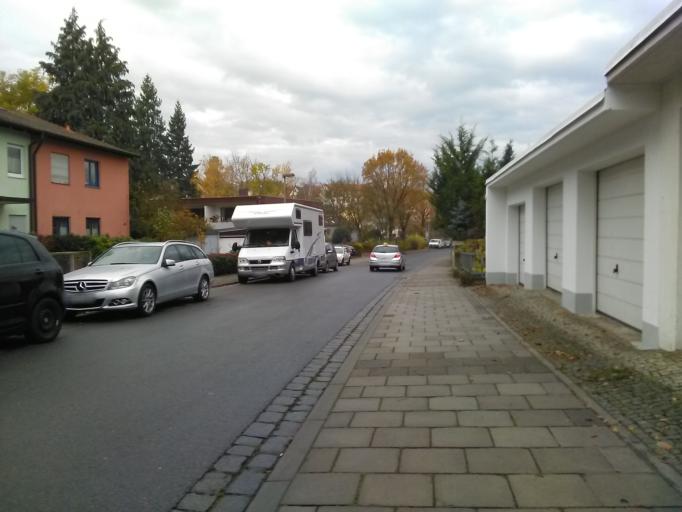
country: DE
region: Bavaria
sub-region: Upper Franconia
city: Bamberg
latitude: 49.8849
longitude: 10.8797
